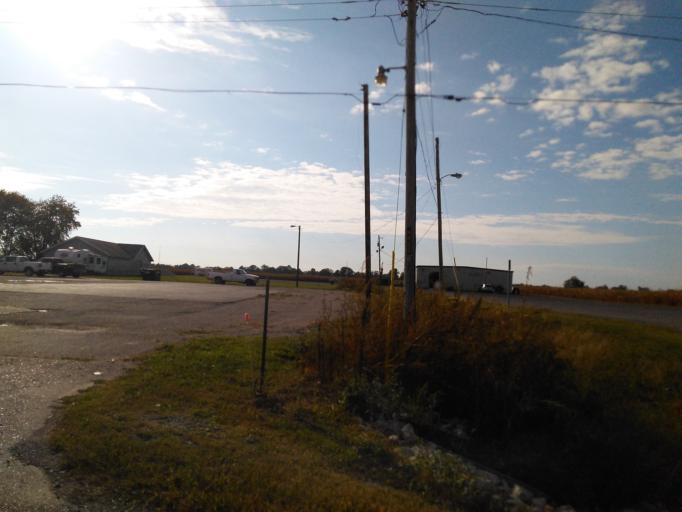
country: US
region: Illinois
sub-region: Bond County
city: Greenville
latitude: 38.8708
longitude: -89.4142
